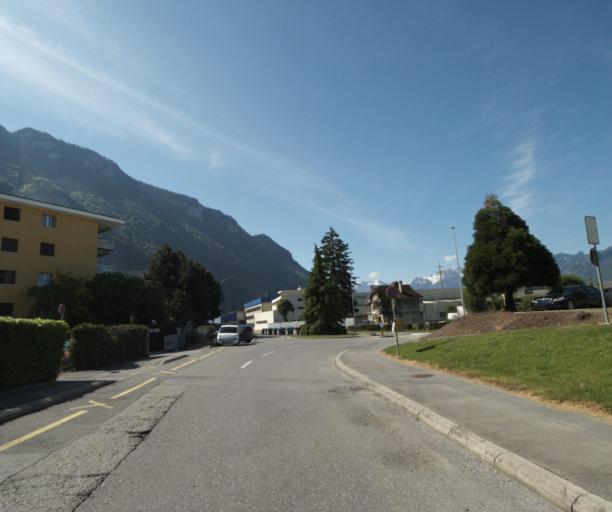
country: CH
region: Vaud
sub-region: Aigle District
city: Villeneuve
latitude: 46.3957
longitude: 6.9343
